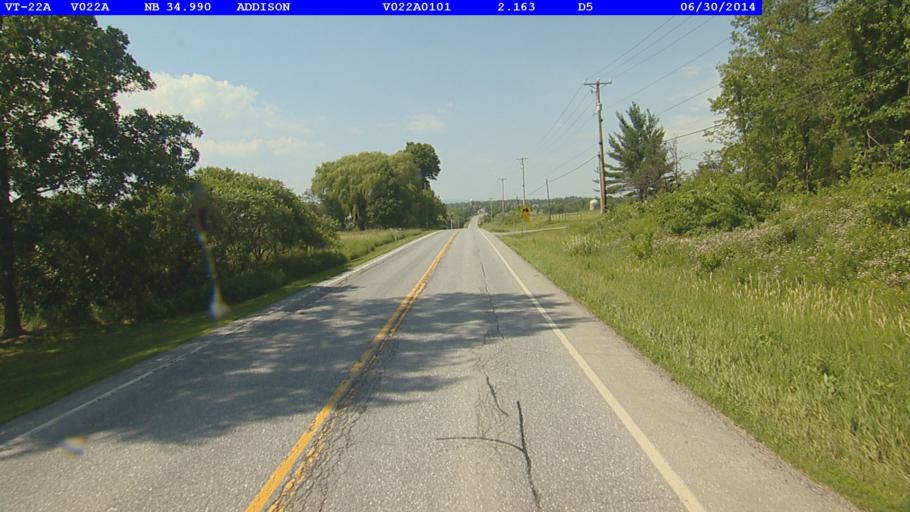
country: US
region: Vermont
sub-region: Addison County
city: Vergennes
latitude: 44.0607
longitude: -73.3027
